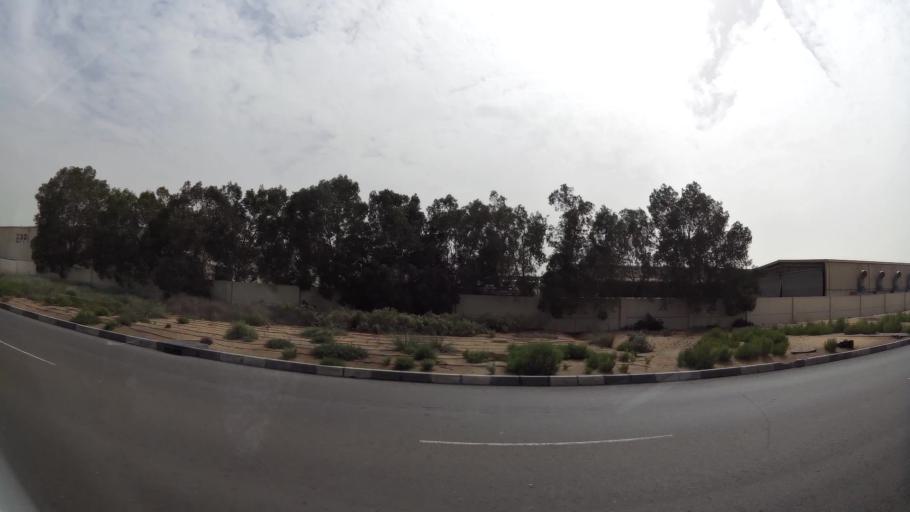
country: AE
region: Abu Dhabi
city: Abu Dhabi
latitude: 24.3237
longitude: 54.5125
